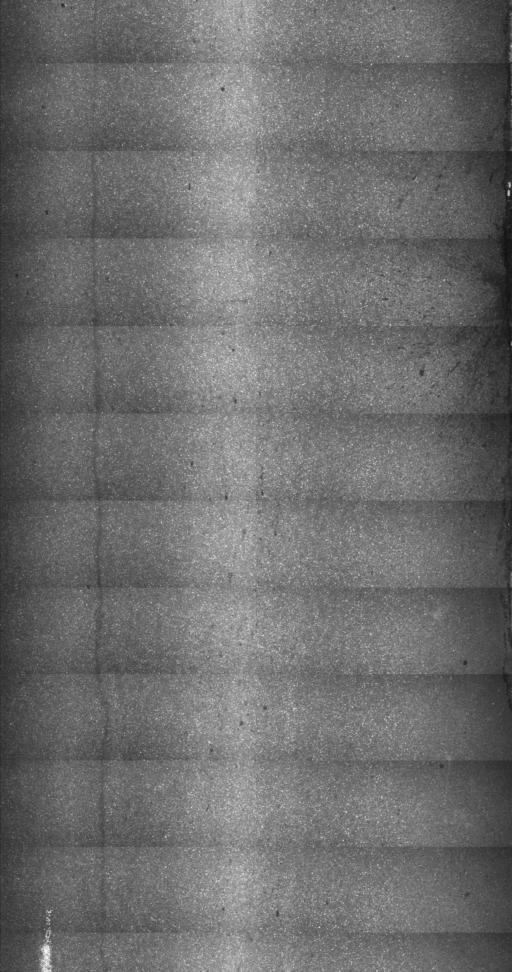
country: US
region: Vermont
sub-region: Chittenden County
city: Burlington
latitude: 44.4626
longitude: -73.2079
